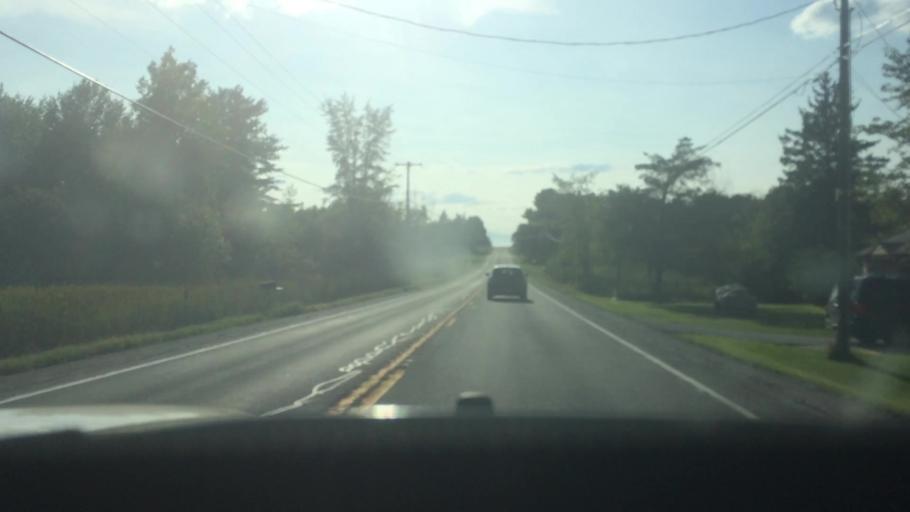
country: US
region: New York
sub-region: St. Lawrence County
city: Potsdam
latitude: 44.6702
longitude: -74.9288
